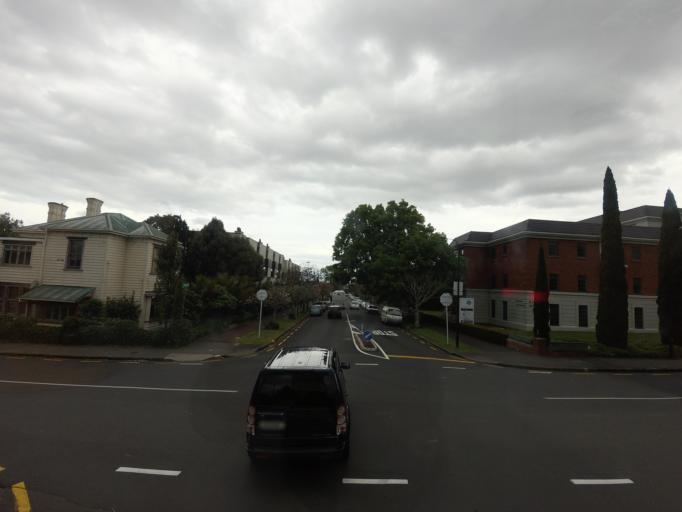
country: NZ
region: Auckland
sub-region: Auckland
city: Auckland
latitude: -36.8618
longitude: 174.7793
